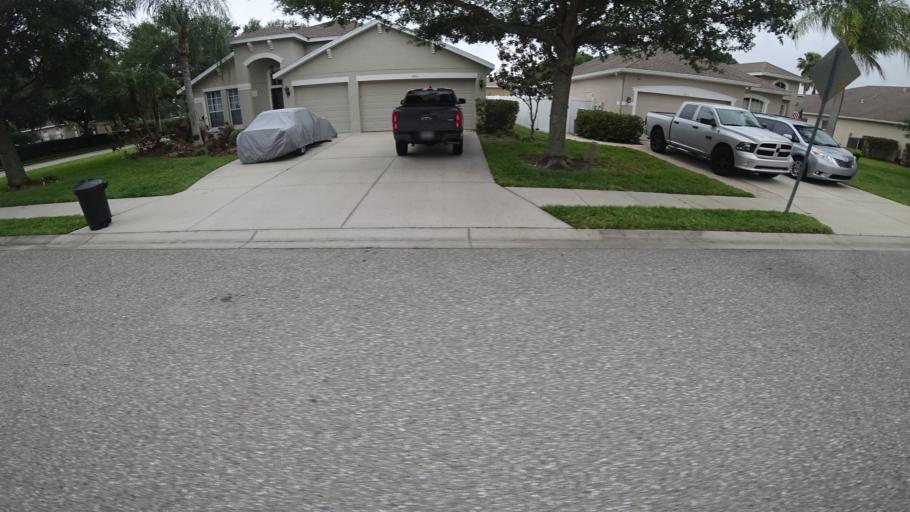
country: US
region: Florida
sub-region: Manatee County
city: Samoset
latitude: 27.4353
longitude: -82.5095
